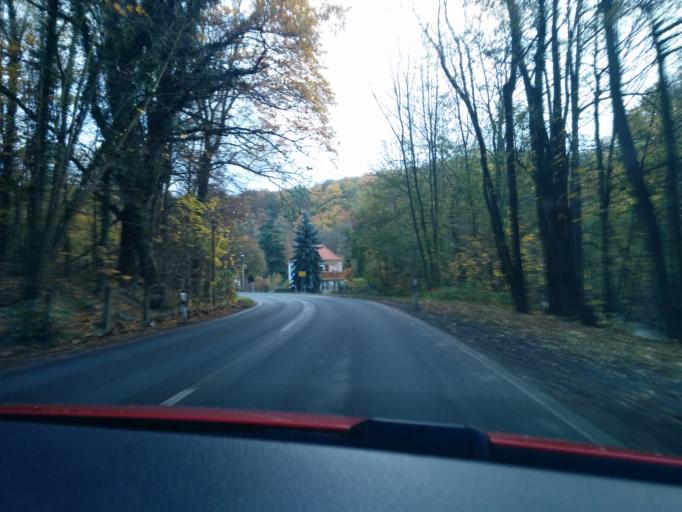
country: DE
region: Saxony
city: Dohna
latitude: 50.9416
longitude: 13.8643
